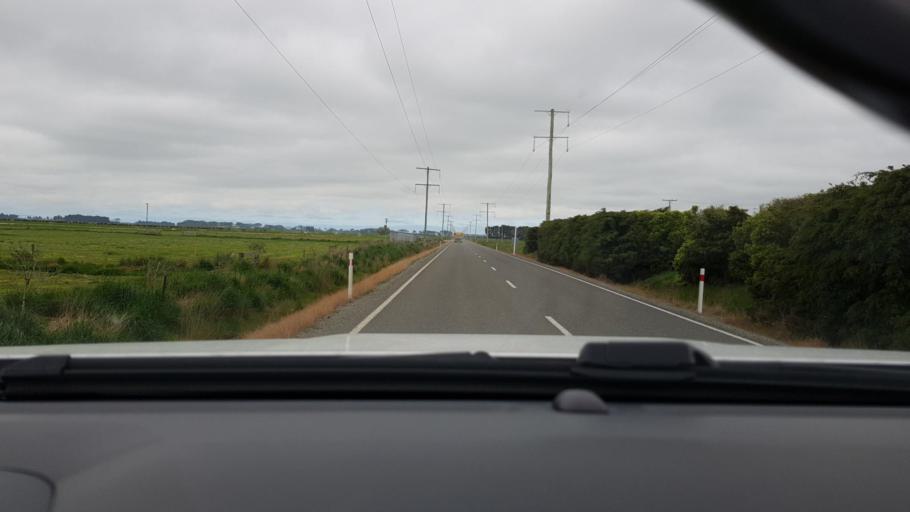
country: NZ
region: Otago
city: Oamaru
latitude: -44.9647
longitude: 170.9800
